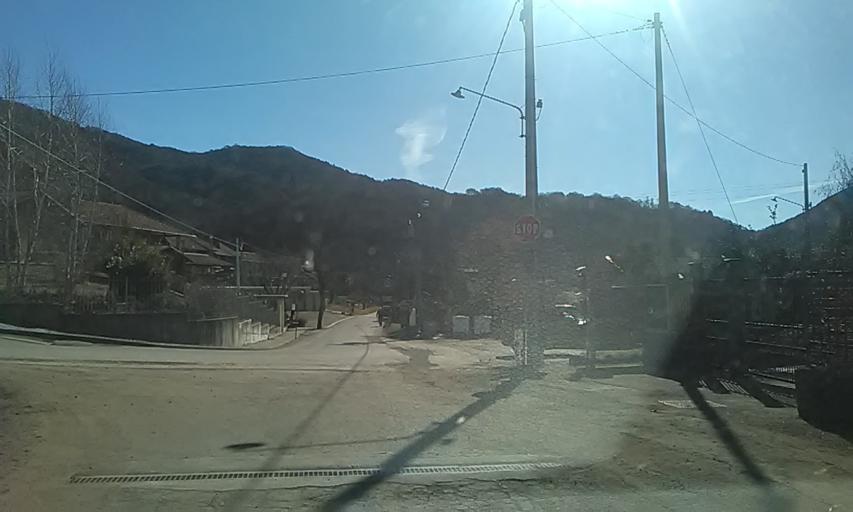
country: IT
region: Piedmont
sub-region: Provincia di Vercelli
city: Breia
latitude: 45.7844
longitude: 8.2926
